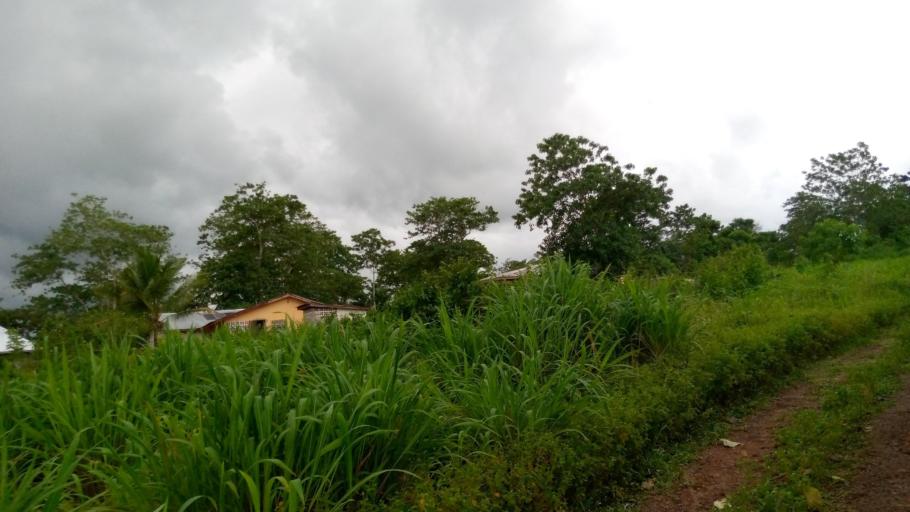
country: SL
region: Southern Province
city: Moyamba
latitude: 8.1627
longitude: -12.4468
